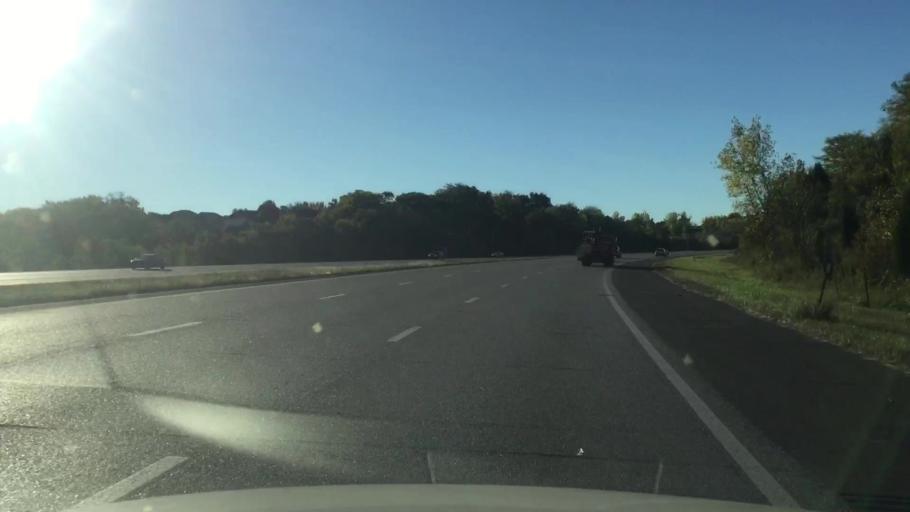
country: US
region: Kansas
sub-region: Johnson County
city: Lenexa
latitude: 38.9916
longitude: -94.7778
